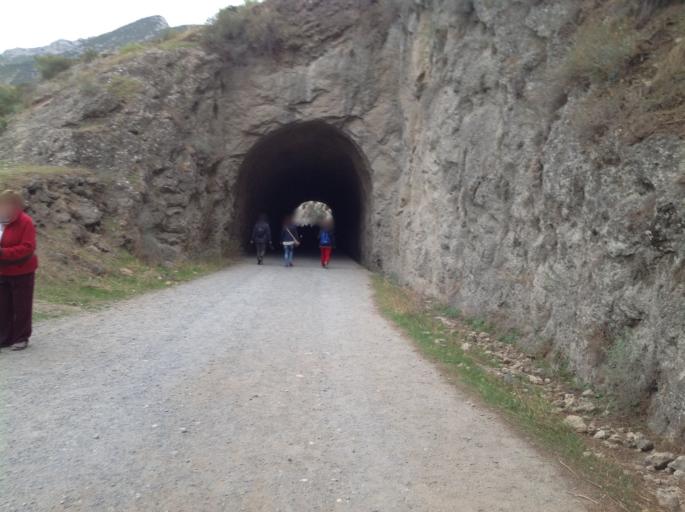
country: ES
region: Andalusia
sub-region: Provincia de Malaga
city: Ardales
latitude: 36.9293
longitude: -4.7940
